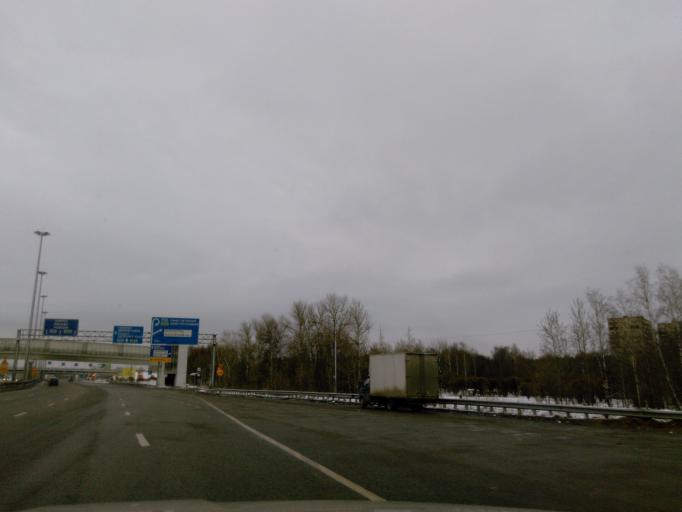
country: RU
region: Moskovskaya
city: Rzhavki
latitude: 56.0026
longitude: 37.2370
